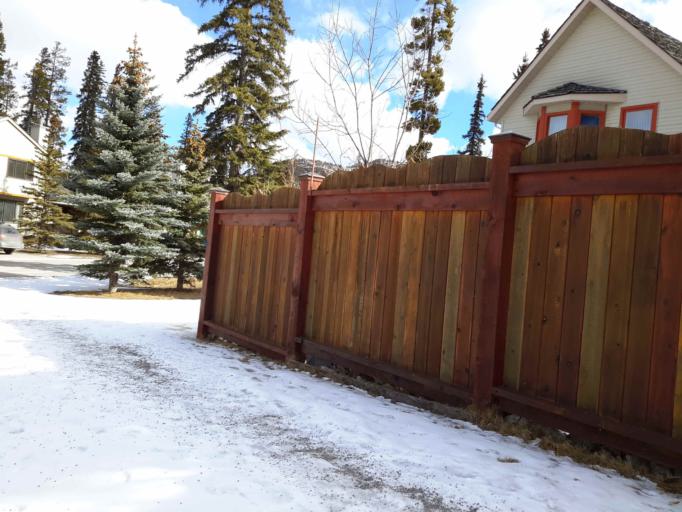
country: CA
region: Alberta
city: Banff
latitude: 51.1688
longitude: -115.5768
